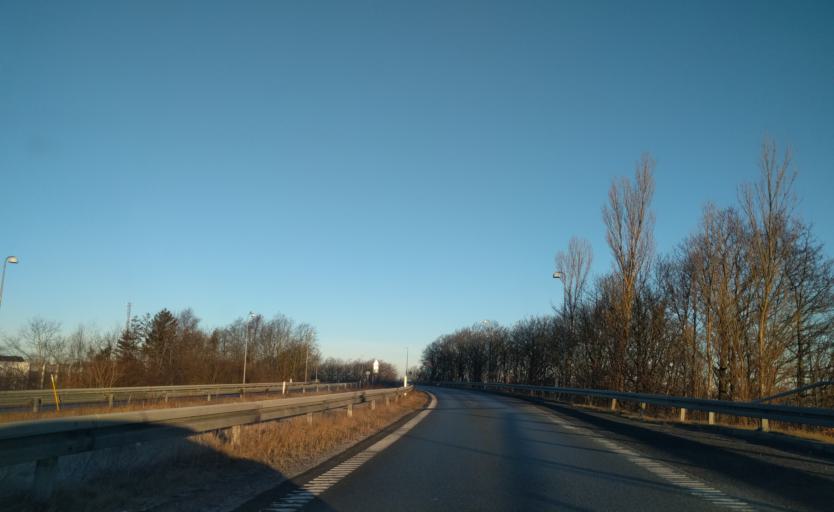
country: DK
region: North Denmark
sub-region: Alborg Kommune
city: Vestbjerg
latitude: 57.0854
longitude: 9.9670
